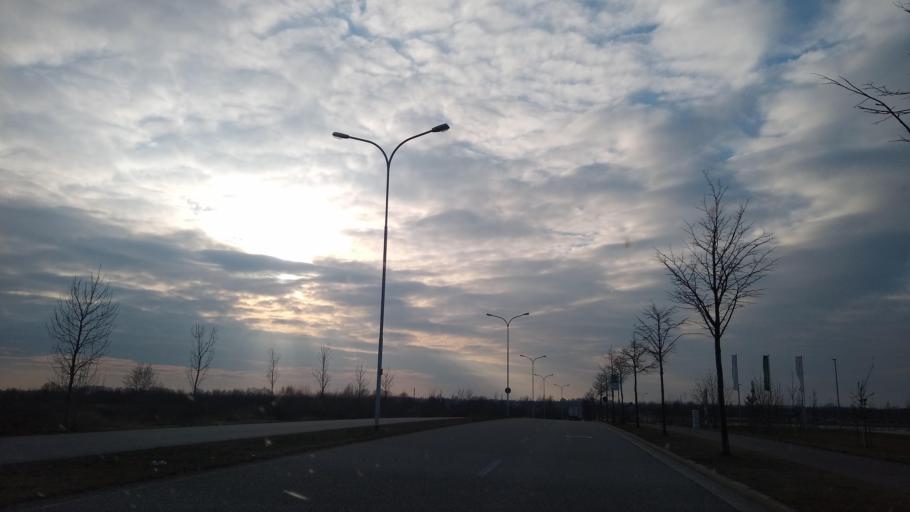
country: DE
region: Saxony-Anhalt
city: Dolbau
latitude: 51.4818
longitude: 12.0795
